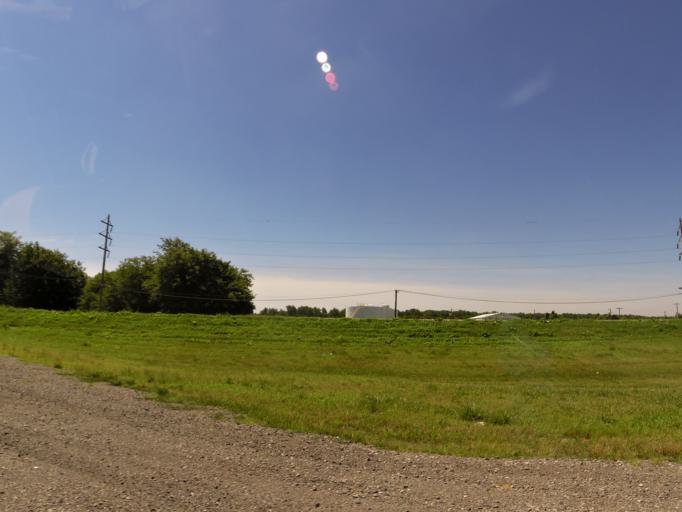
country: US
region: Missouri
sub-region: New Madrid County
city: New Madrid
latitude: 36.5814
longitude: -89.5547
